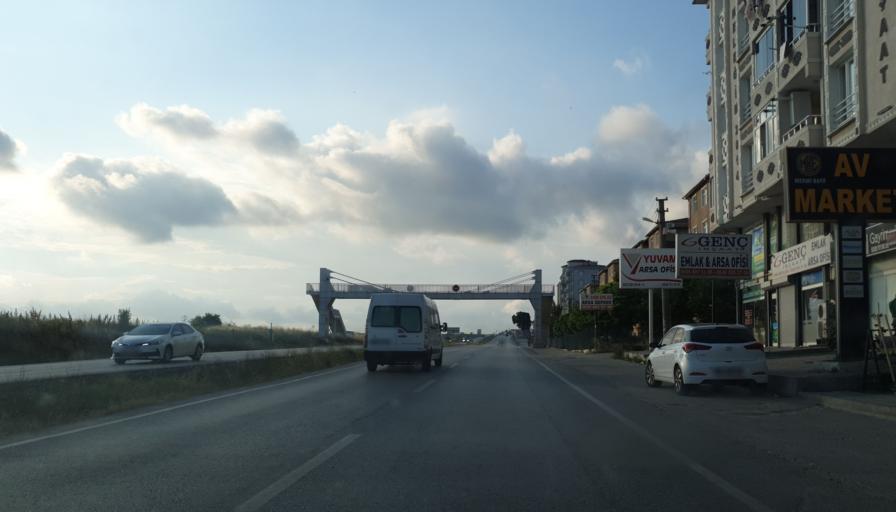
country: TR
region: Tekirdag
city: Cerkezkoey
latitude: 41.3336
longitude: 27.9691
